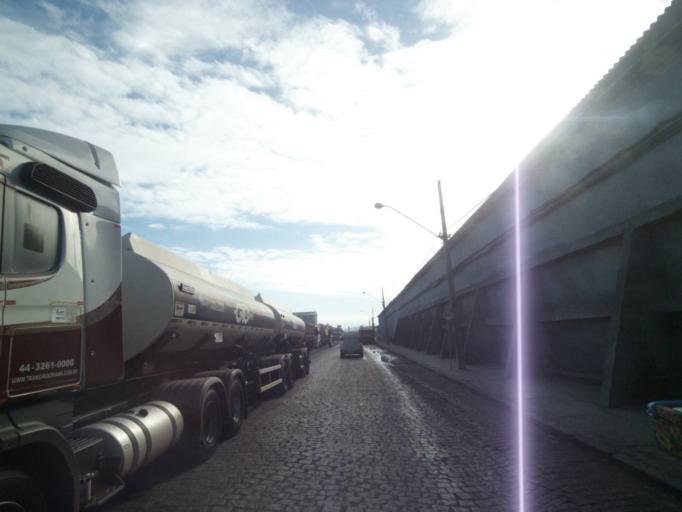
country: BR
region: Parana
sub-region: Paranagua
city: Paranagua
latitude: -25.5172
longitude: -48.5259
